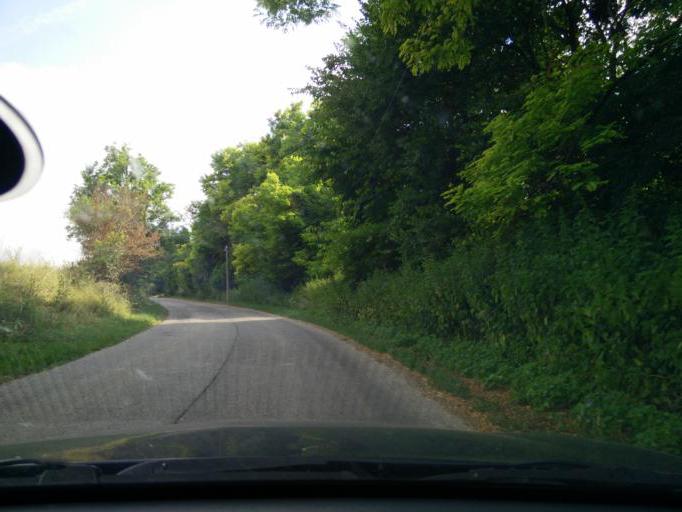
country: HU
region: Komarom-Esztergom
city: Sutto
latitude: 47.7162
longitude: 18.4511
